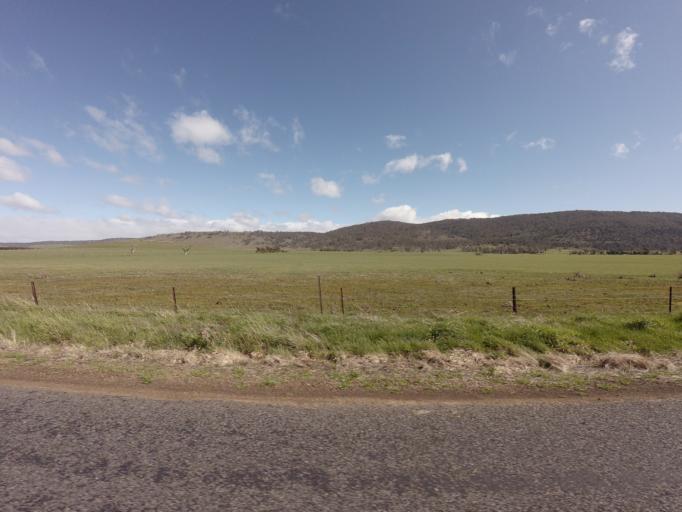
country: AU
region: Tasmania
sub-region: Northern Midlands
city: Evandale
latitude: -41.9877
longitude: 147.4514
